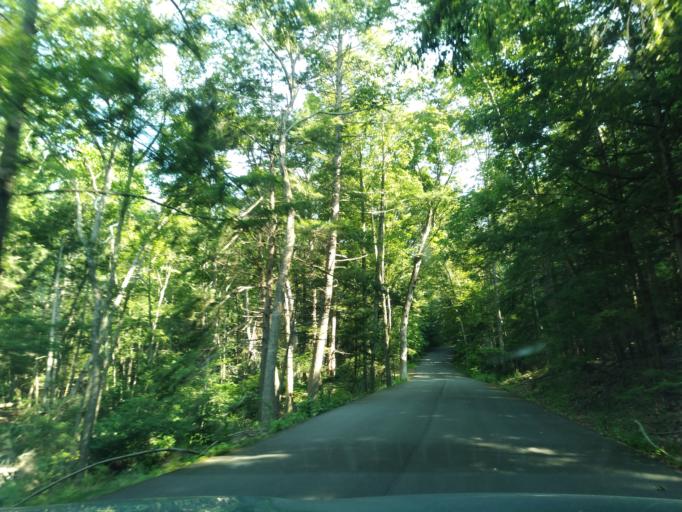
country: US
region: Connecticut
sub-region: New Haven County
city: Southbury
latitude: 41.4260
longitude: -73.2055
